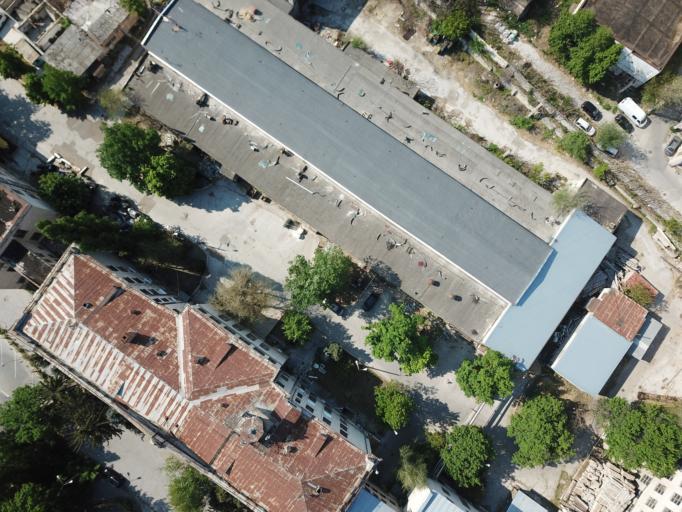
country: MD
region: Chisinau
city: Chisinau
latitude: 47.0105
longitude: 28.8557
